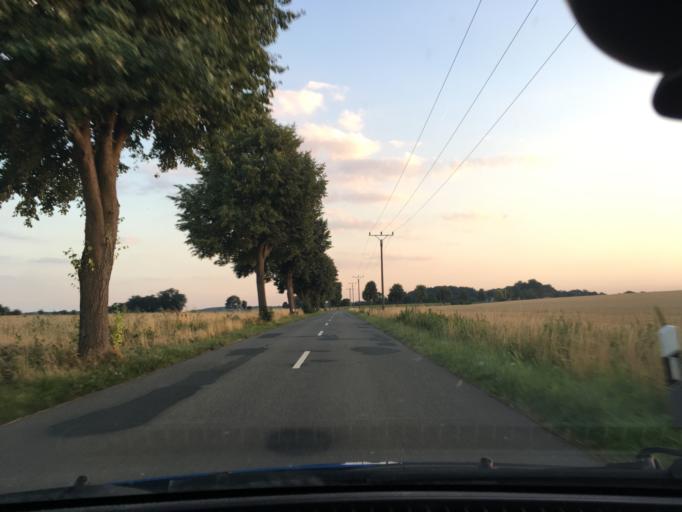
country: DE
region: Lower Saxony
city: Natendorf
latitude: 53.1040
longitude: 10.4528
